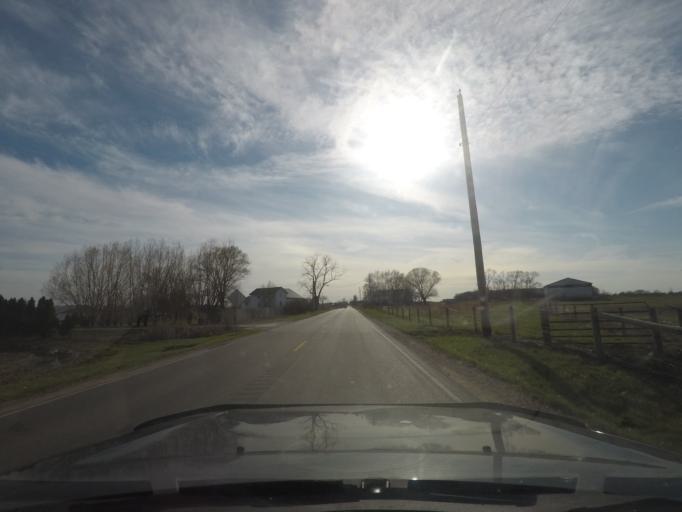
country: US
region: Indiana
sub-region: Elkhart County
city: Wakarusa
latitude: 41.5154
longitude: -85.9804
